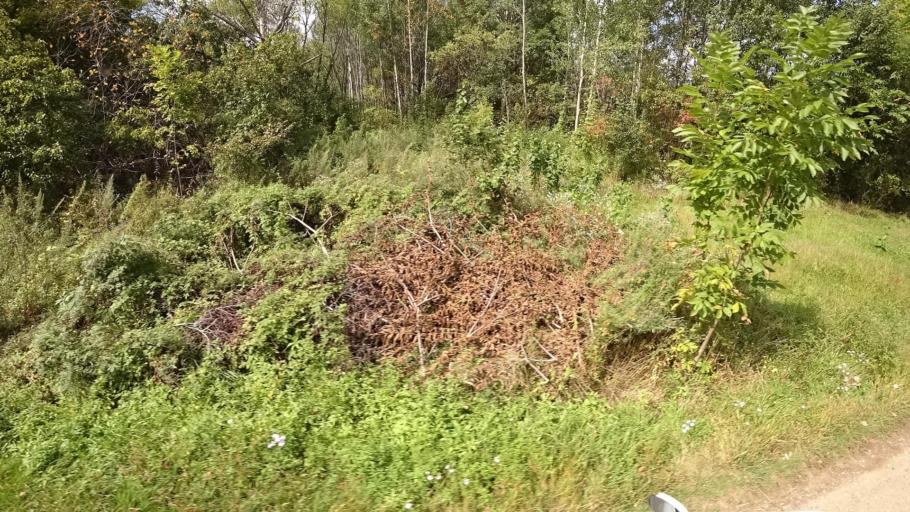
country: RU
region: Primorskiy
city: Yakovlevka
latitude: 44.7090
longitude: 133.6291
